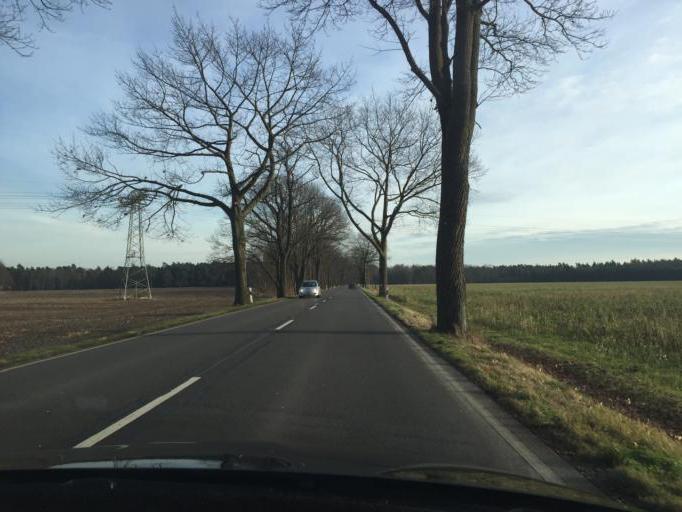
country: DE
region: Brandenburg
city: Cottbus
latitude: 51.7459
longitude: 14.3826
